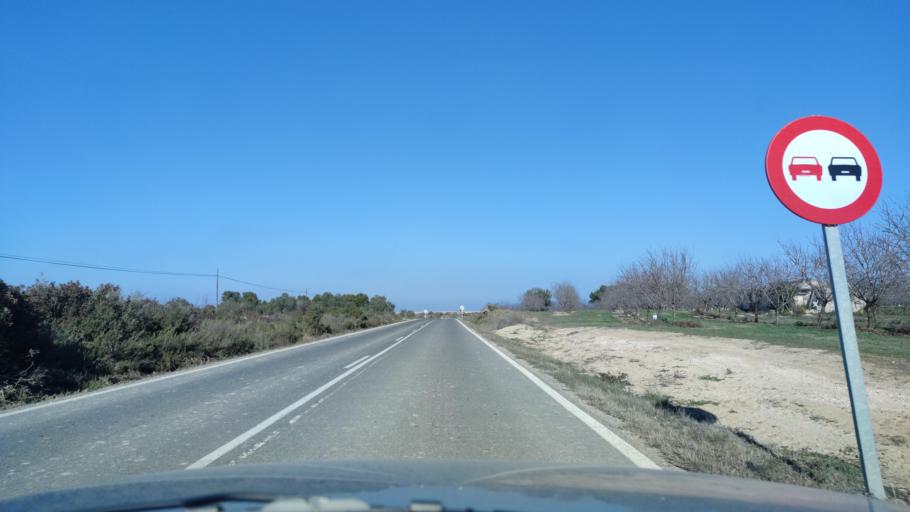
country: ES
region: Catalonia
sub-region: Provincia de Lleida
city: Maials
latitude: 41.3481
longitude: 0.4693
